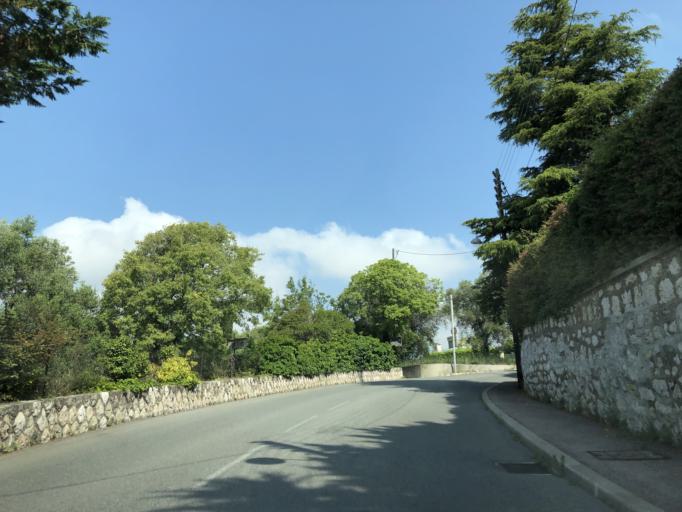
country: FR
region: Provence-Alpes-Cote d'Azur
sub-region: Departement des Alpes-Maritimes
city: Saint-Andre-de-la-Roche
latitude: 43.7258
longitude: 7.2949
